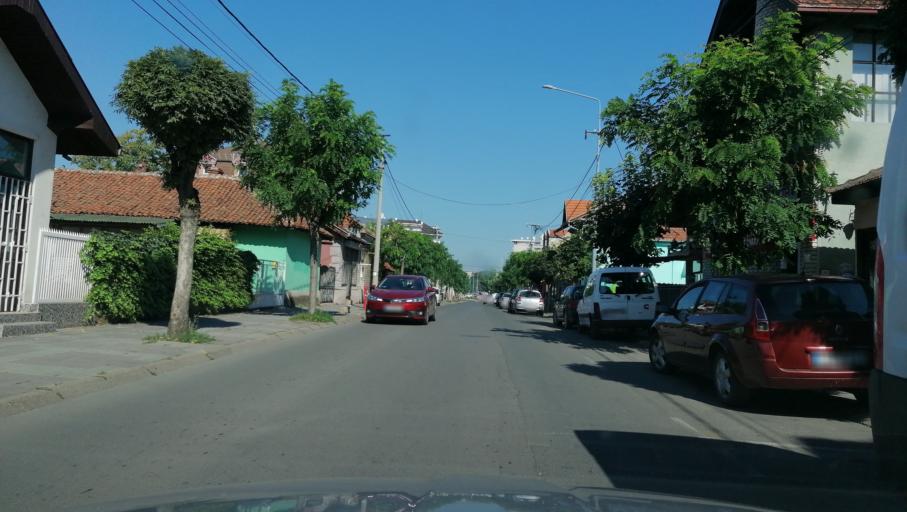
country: RS
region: Central Serbia
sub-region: Rasinski Okrug
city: Krusevac
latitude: 43.5748
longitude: 21.3357
